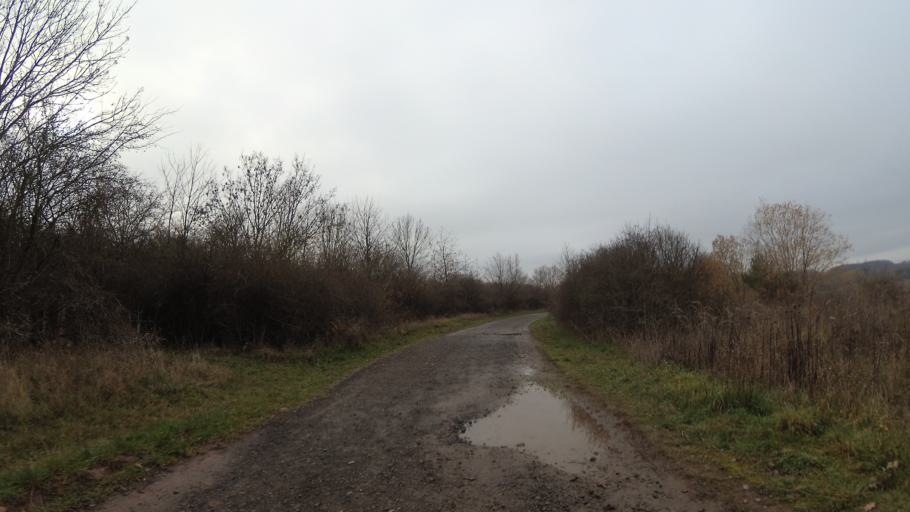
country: DE
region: Saarland
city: Merchweiler
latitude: 49.3549
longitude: 7.0363
